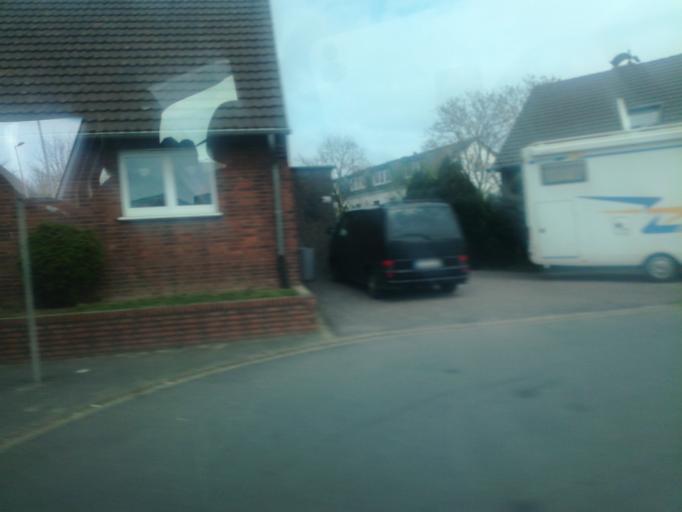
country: DE
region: North Rhine-Westphalia
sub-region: Regierungsbezirk Dusseldorf
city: Kamp-Lintfort
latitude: 51.5085
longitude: 6.5438
